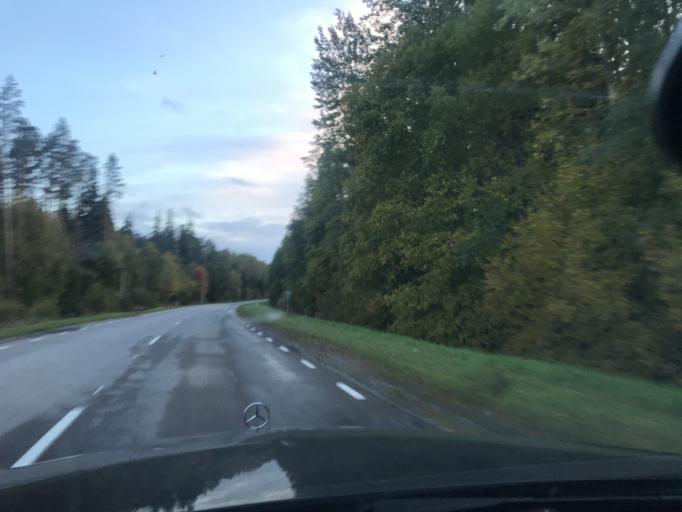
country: EE
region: Valgamaa
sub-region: Torva linn
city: Torva
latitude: 57.9988
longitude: 26.0789
